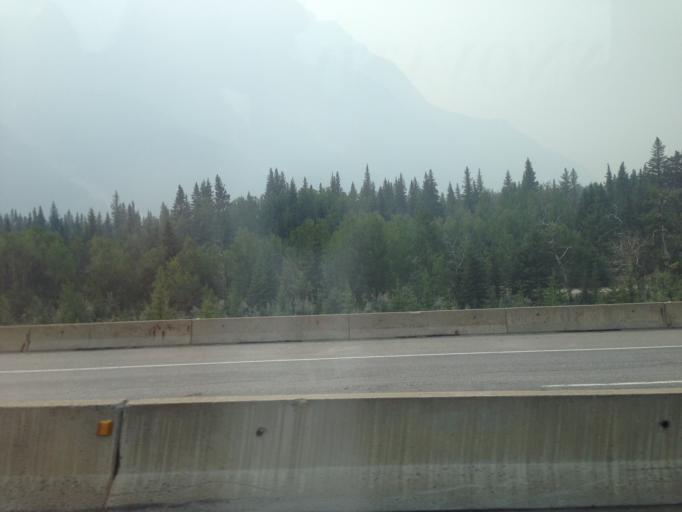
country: CA
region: Alberta
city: Banff
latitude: 51.1722
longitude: -115.4689
